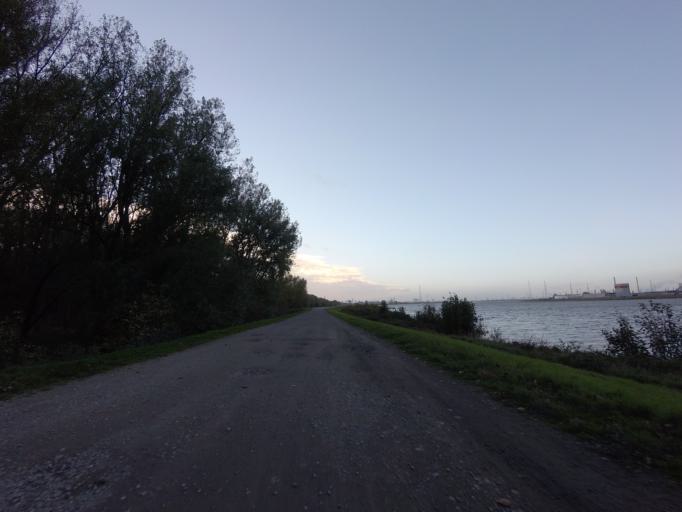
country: BE
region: Flanders
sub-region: Provincie Antwerpen
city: Antwerpen
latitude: 51.2361
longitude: 4.3672
